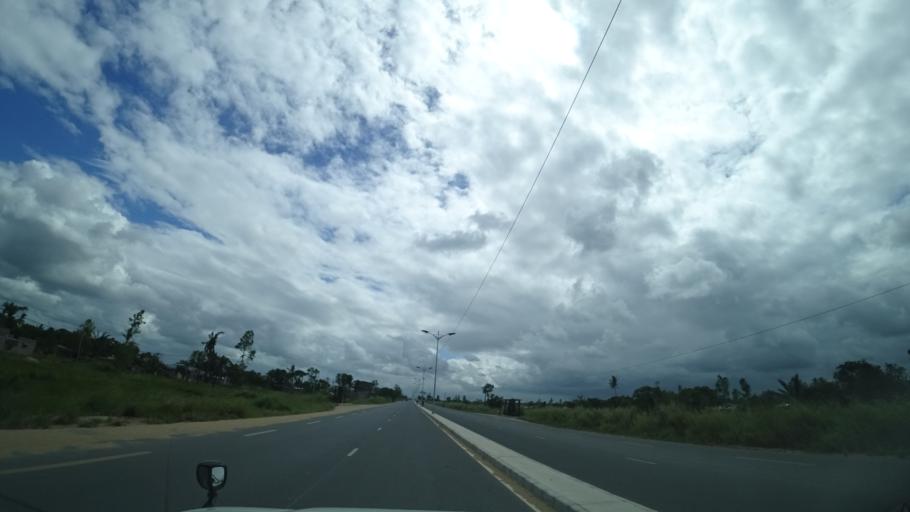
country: MZ
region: Sofala
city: Dondo
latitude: -19.5993
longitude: 34.7404
